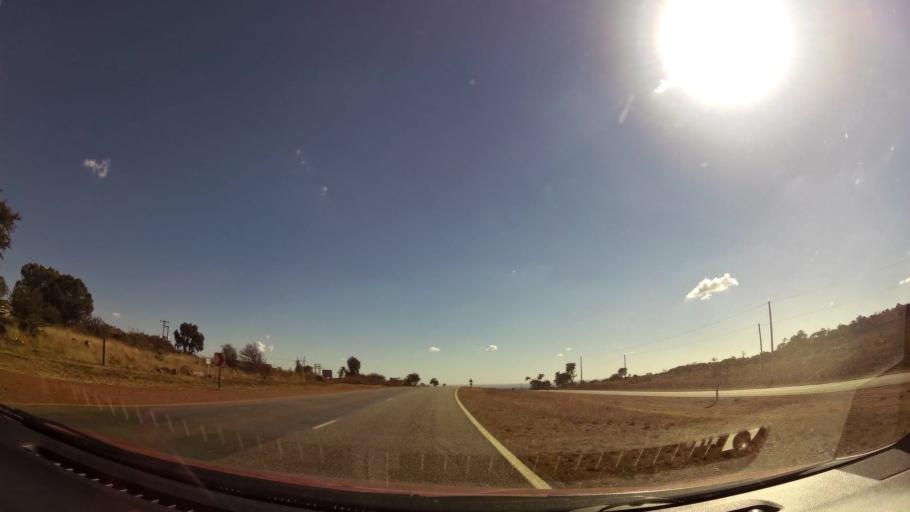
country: ZA
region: Gauteng
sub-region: West Rand District Municipality
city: Carletonville
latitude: -26.4173
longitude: 27.4404
